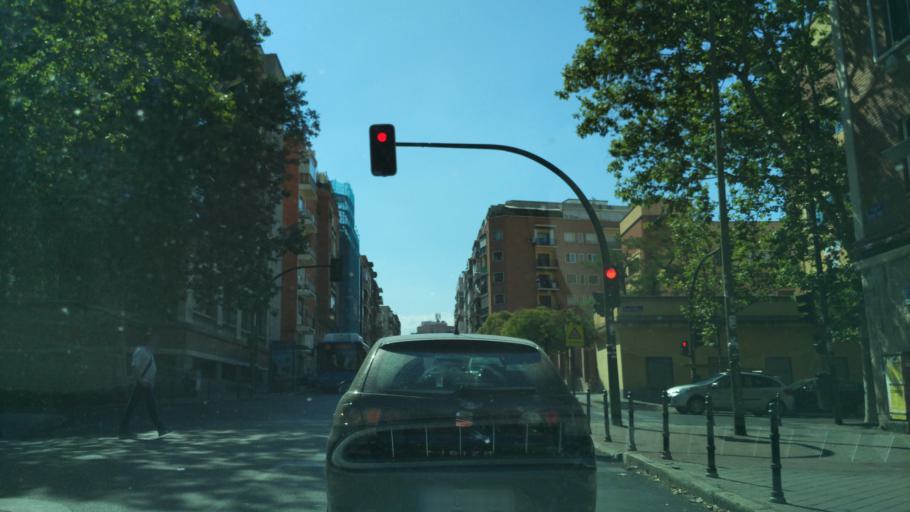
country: ES
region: Madrid
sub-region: Provincia de Madrid
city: Tetuan de las Victorias
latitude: 40.4567
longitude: -3.6977
